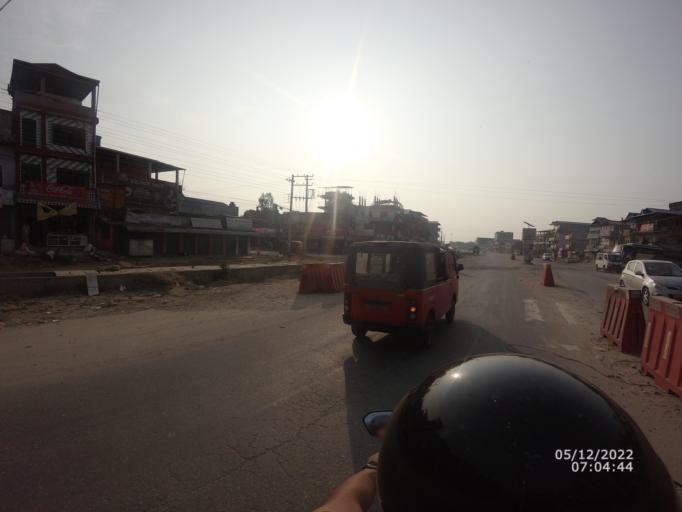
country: NP
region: Central Region
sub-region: Narayani Zone
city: Bharatpur
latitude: 27.6713
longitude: 84.4352
